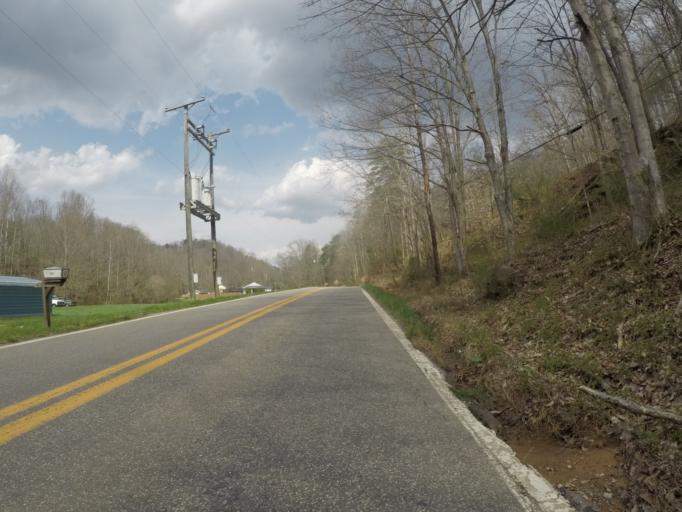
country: US
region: West Virginia
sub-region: Cabell County
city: Pea Ridge
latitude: 38.3348
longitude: -82.3388
